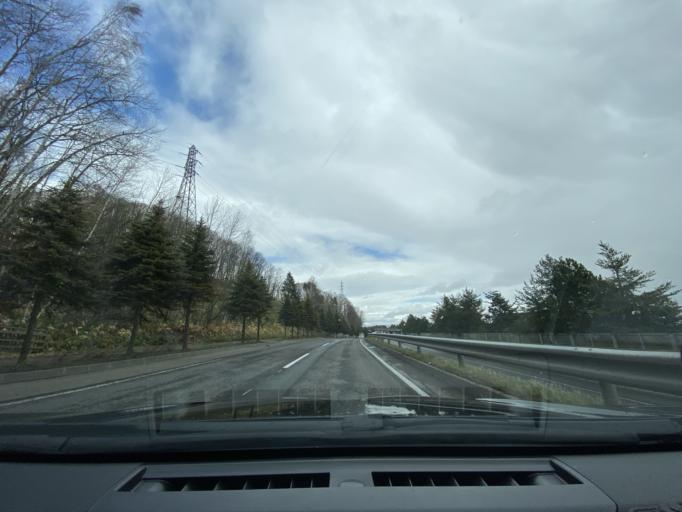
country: JP
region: Hokkaido
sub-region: Asahikawa-shi
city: Asahikawa
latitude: 43.8115
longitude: 142.3638
